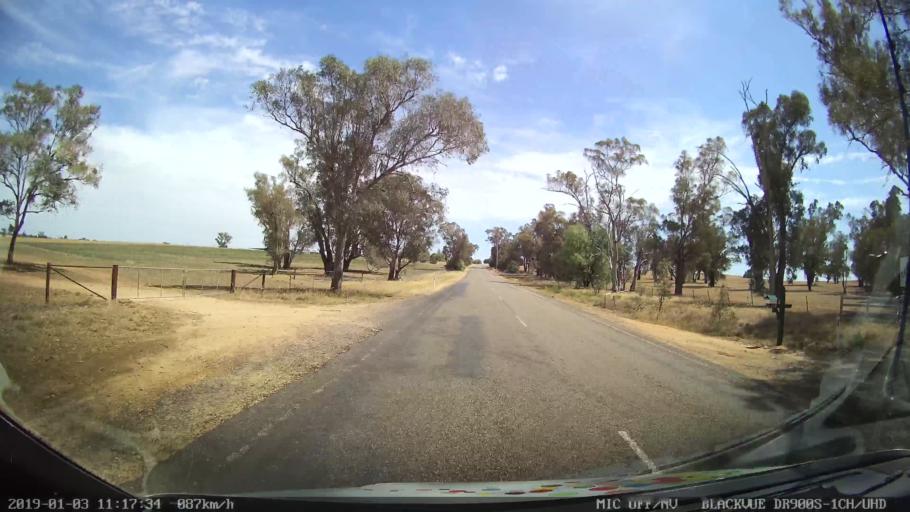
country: AU
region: New South Wales
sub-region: Young
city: Young
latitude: -34.1371
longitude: 148.2654
